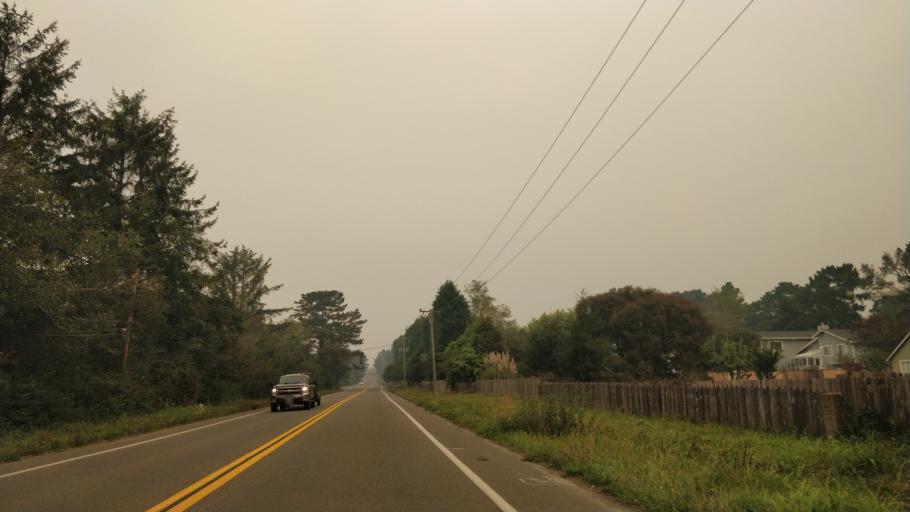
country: US
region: California
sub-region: Humboldt County
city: McKinleyville
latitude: 40.9581
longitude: -124.1008
